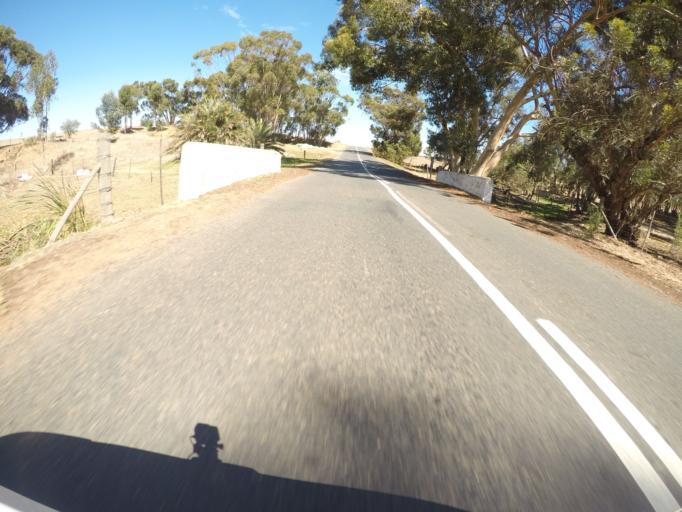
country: ZA
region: Western Cape
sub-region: City of Cape Town
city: Atlantis
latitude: -33.6997
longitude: 18.5888
